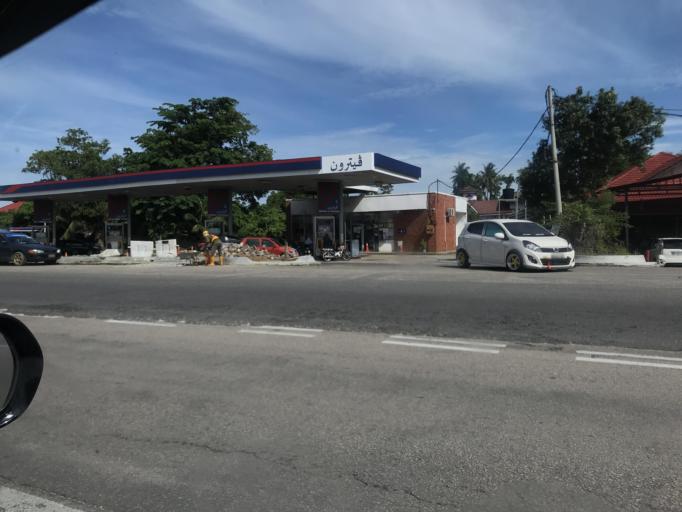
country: MY
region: Kelantan
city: Kota Bharu
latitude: 6.1209
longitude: 102.1980
